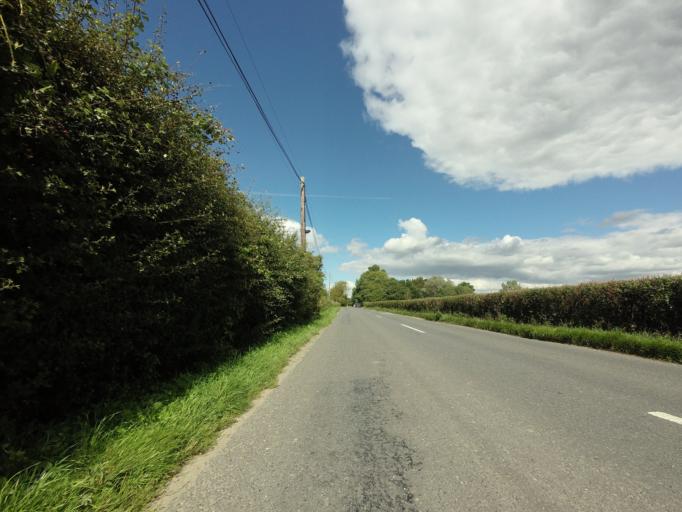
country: GB
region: England
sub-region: Kent
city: Marden
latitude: 51.1545
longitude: 0.4847
